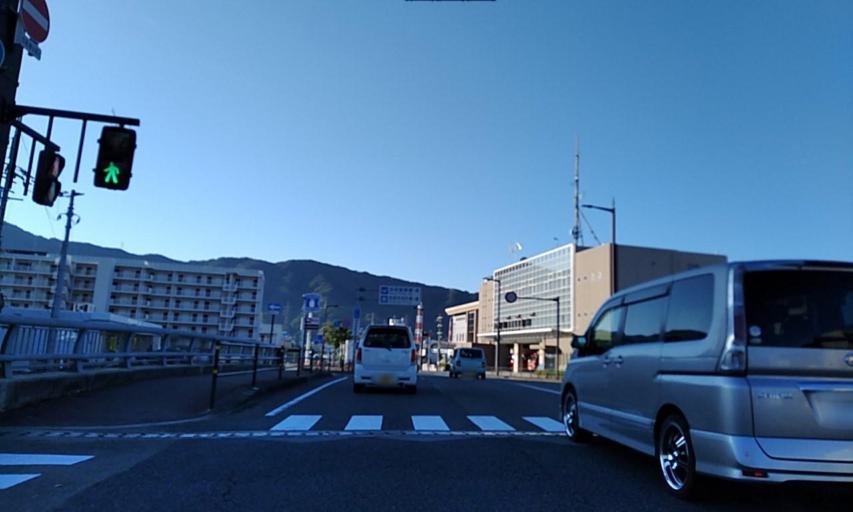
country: JP
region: Wakayama
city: Kainan
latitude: 34.1574
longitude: 135.2056
